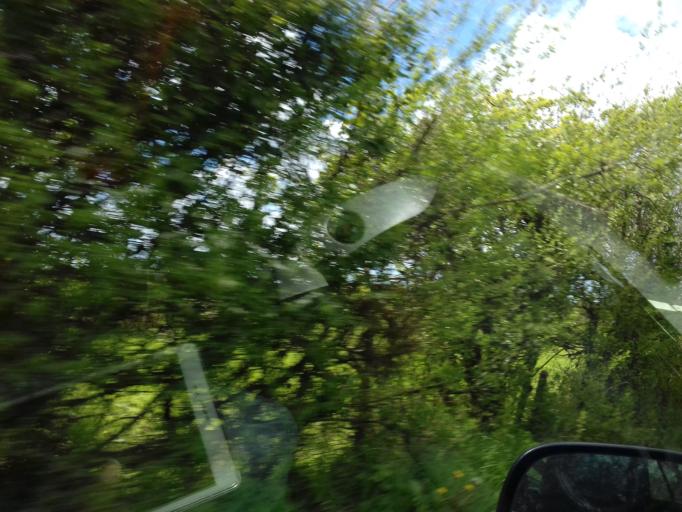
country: IE
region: Leinster
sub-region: Loch Garman
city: Loch Garman
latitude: 52.3107
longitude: -6.5396
